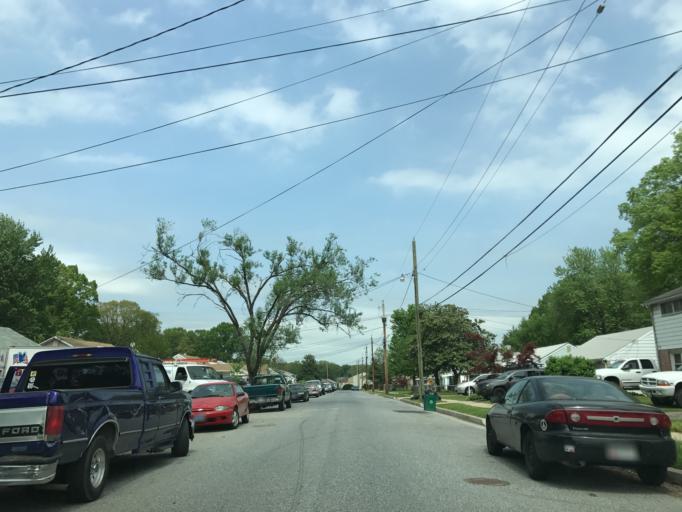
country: US
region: Maryland
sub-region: Baltimore County
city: Middle River
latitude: 39.3104
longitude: -76.4436
